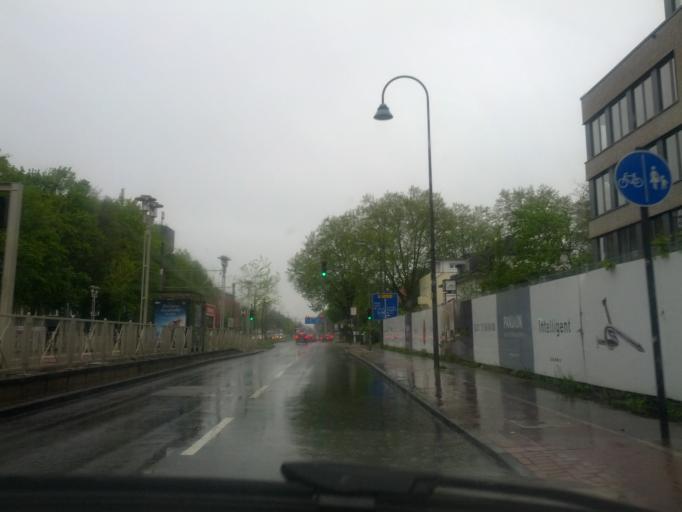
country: DE
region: North Rhine-Westphalia
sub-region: Regierungsbezirk Koln
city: Mengenich
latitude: 50.9381
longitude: 6.8553
